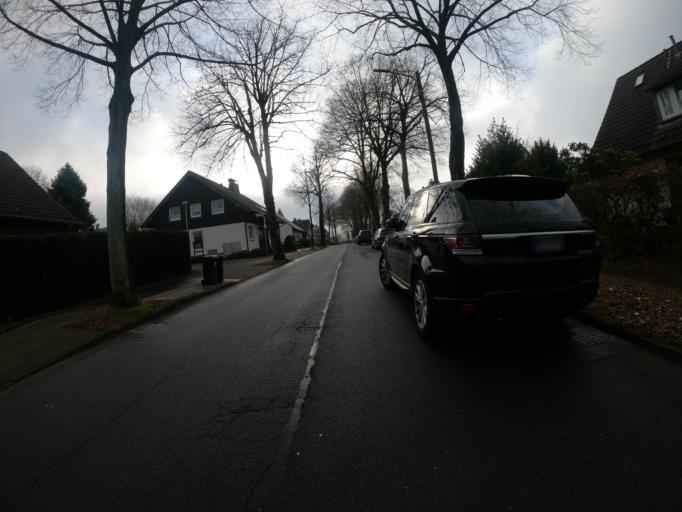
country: DE
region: North Rhine-Westphalia
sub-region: Regierungsbezirk Dusseldorf
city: Wuppertal
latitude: 51.2311
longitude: 7.1350
